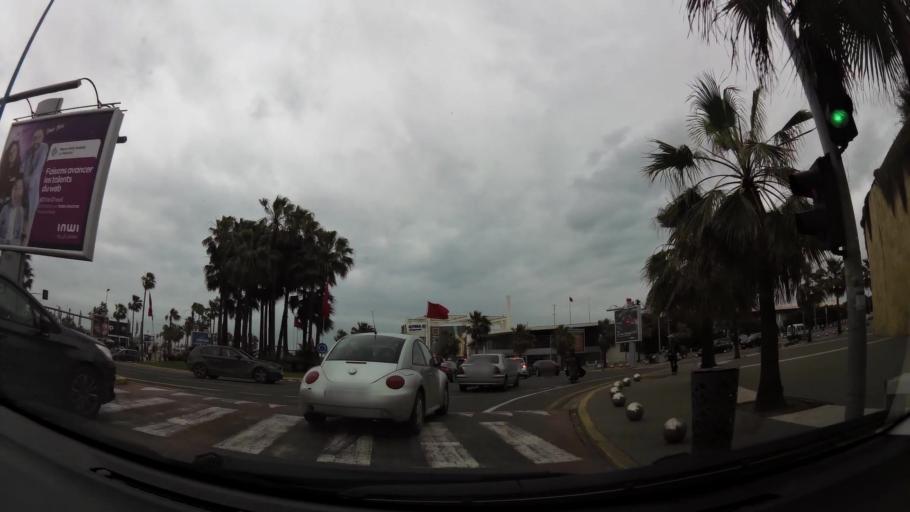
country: MA
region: Grand Casablanca
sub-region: Casablanca
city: Casablanca
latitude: 33.5951
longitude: -7.6678
